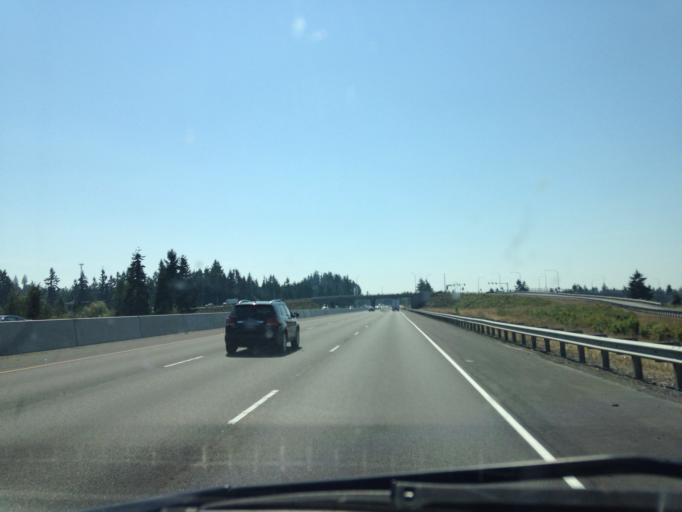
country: US
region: Washington
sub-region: Thurston County
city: Grand Mound
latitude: 46.8059
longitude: -123.0053
